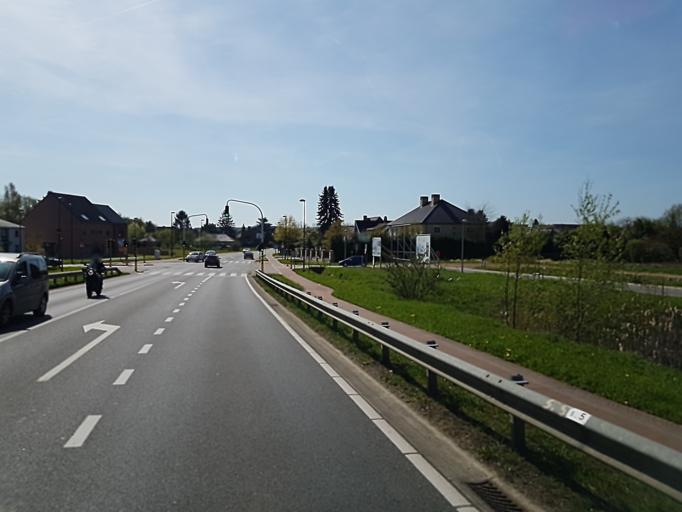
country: BE
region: Flanders
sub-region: Provincie Vlaams-Brabant
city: Aarschot
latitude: 50.9968
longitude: 4.8425
